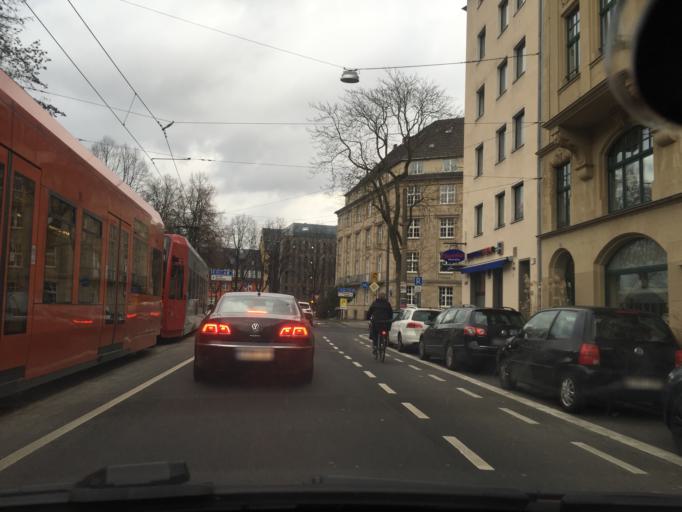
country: DE
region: North Rhine-Westphalia
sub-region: Regierungsbezirk Koln
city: Bayenthal
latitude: 50.9219
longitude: 6.9659
